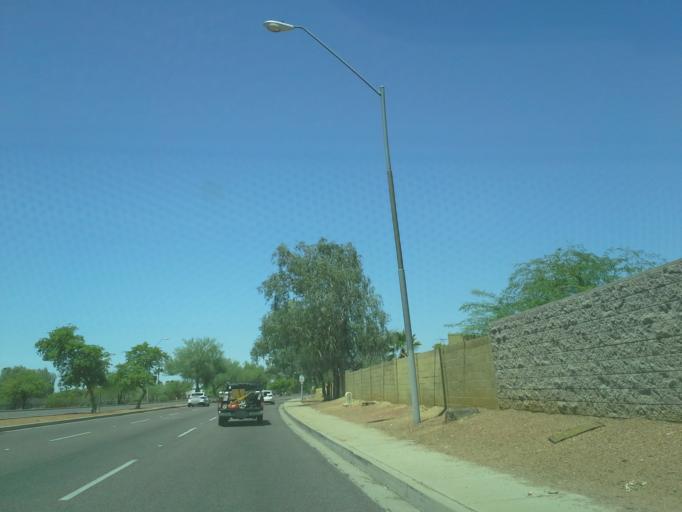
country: US
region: Arizona
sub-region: Maricopa County
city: Paradise Valley
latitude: 33.6332
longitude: -112.0406
